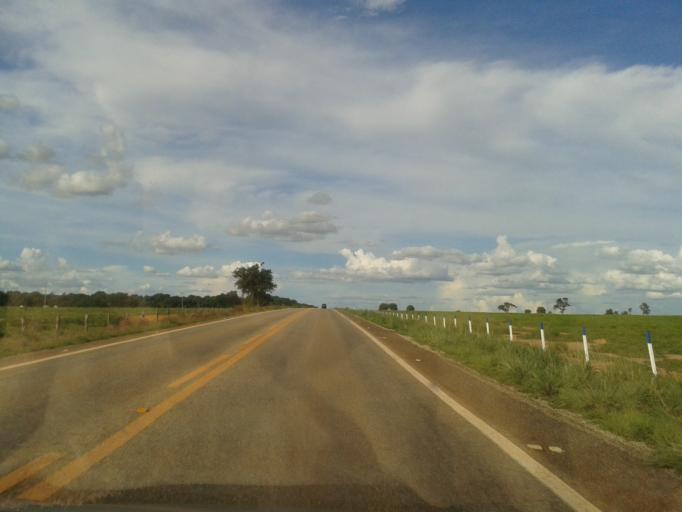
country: BR
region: Goias
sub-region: Mozarlandia
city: Mozarlandia
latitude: -14.3396
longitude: -50.4177
